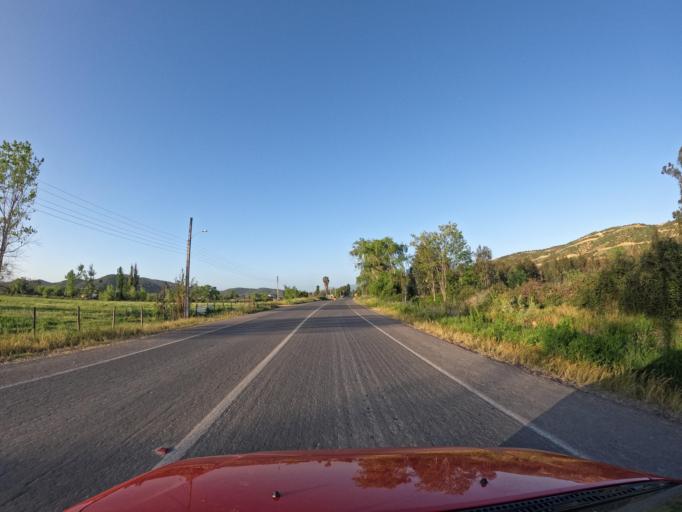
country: CL
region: O'Higgins
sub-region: Provincia de Colchagua
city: Santa Cruz
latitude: -34.3424
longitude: -71.4042
